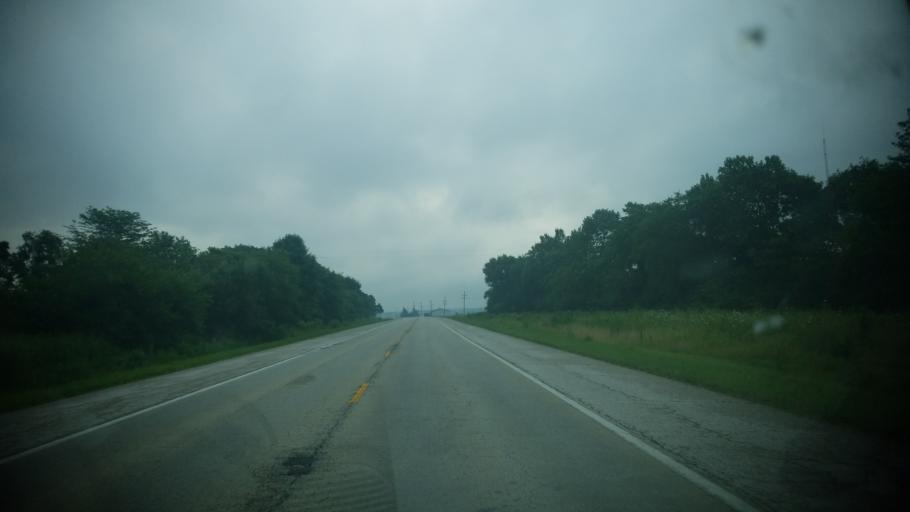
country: US
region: Illinois
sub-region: Clay County
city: Flora
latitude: 38.6775
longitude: -88.3960
